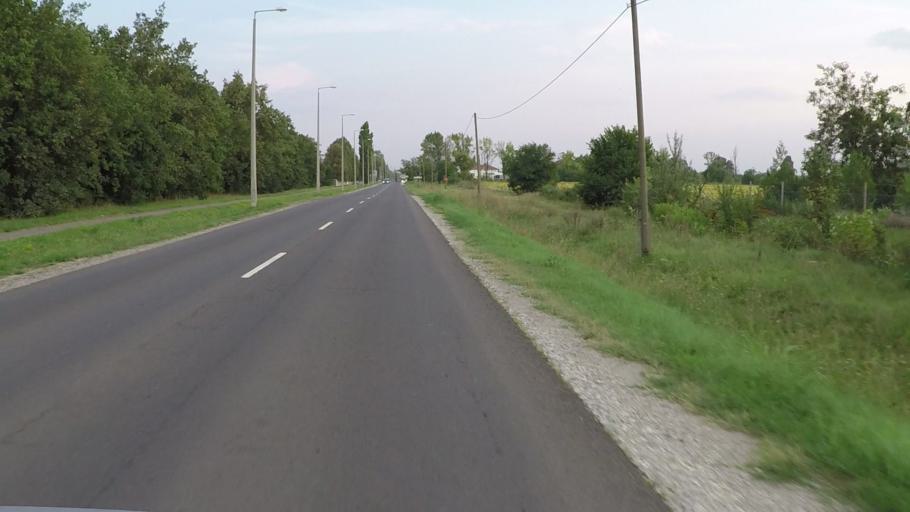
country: HU
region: Jasz-Nagykun-Szolnok
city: Szolnok
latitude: 47.1923
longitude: 20.1571
